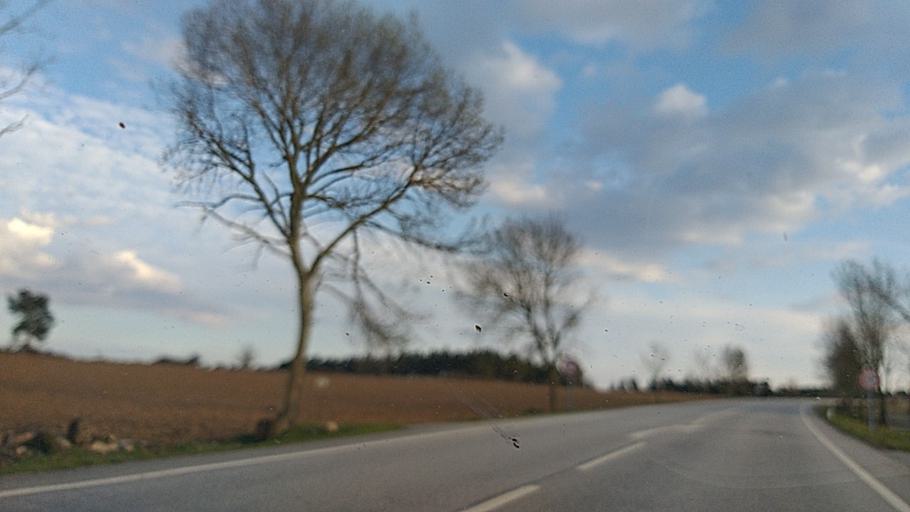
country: PT
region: Guarda
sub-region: Pinhel
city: Pinhel
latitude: 40.6585
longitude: -6.9673
